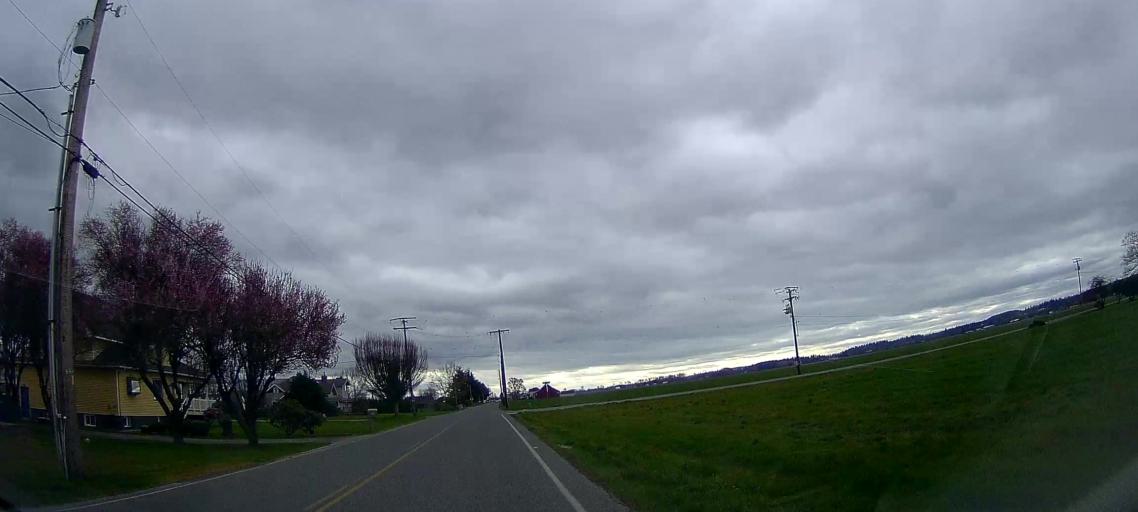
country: US
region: Washington
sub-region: Skagit County
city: Mount Vernon
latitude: 48.3998
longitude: -122.4010
